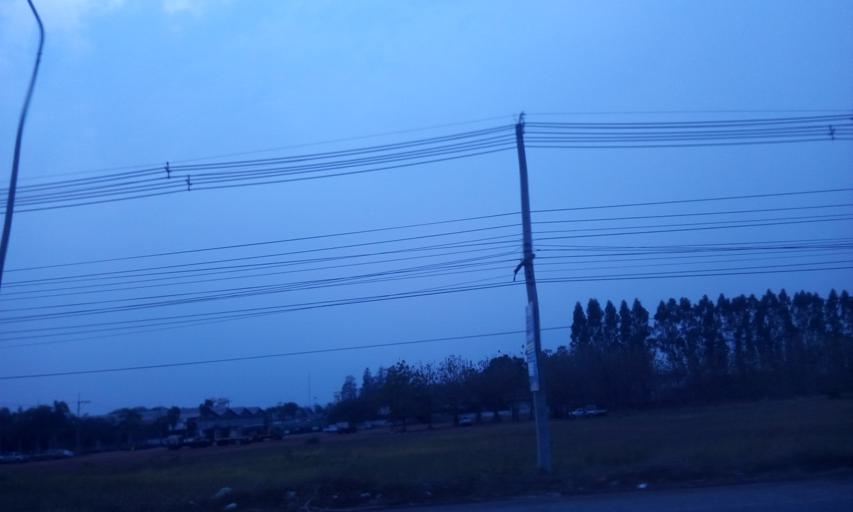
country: TH
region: Chon Buri
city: Ko Chan
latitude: 13.2953
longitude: 101.2600
